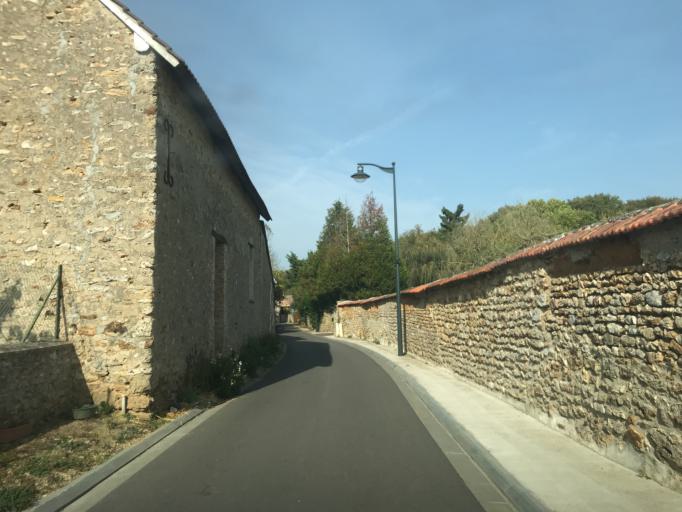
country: FR
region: Haute-Normandie
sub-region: Departement de l'Eure
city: La Chapelle-Reanville
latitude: 49.0799
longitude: 1.3919
